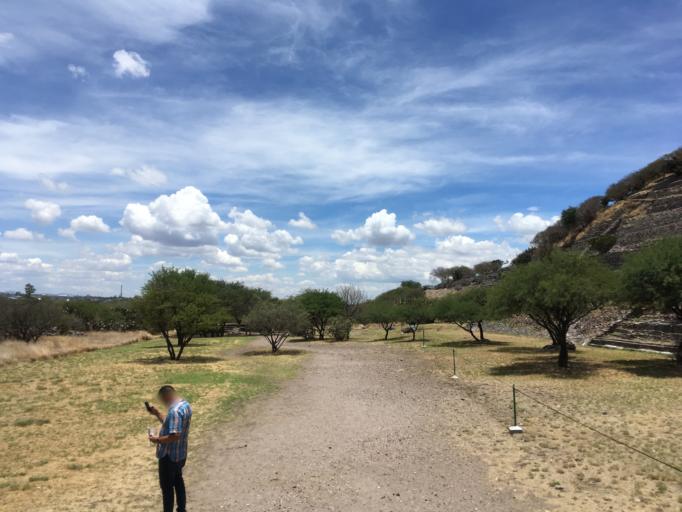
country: MX
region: Queretaro
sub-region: Corregidora
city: El Pueblito
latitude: 20.5506
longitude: -100.4431
